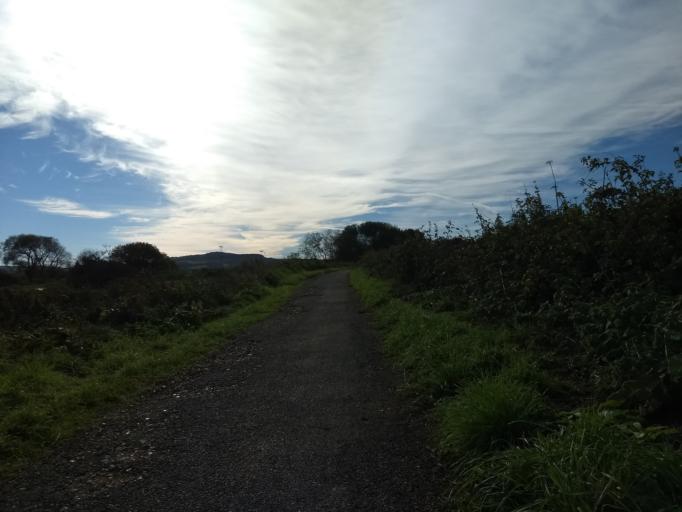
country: GB
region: England
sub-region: Isle of Wight
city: Newchurch
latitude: 50.6571
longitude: -1.2420
